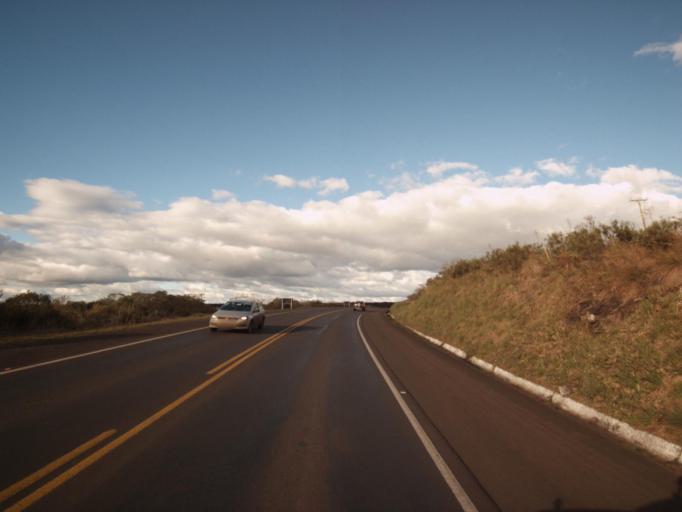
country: BR
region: Santa Catarina
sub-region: Campos Novos
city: Campos Novos
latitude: -27.3589
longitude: -51.3232
